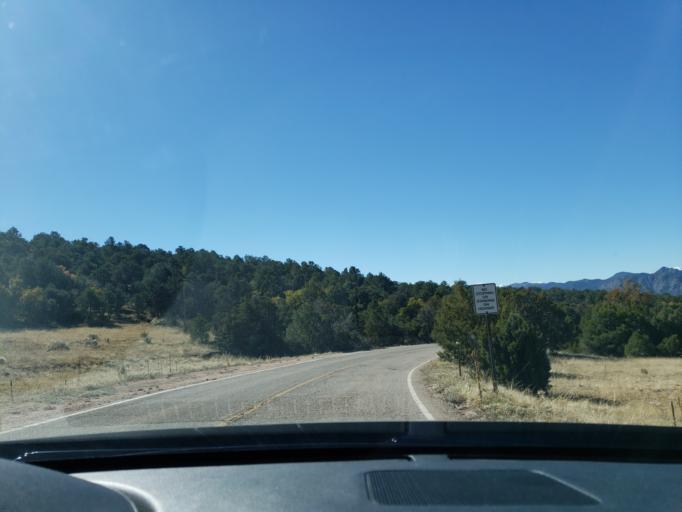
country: US
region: Colorado
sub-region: Fremont County
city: Canon City
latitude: 38.4644
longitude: -105.3117
